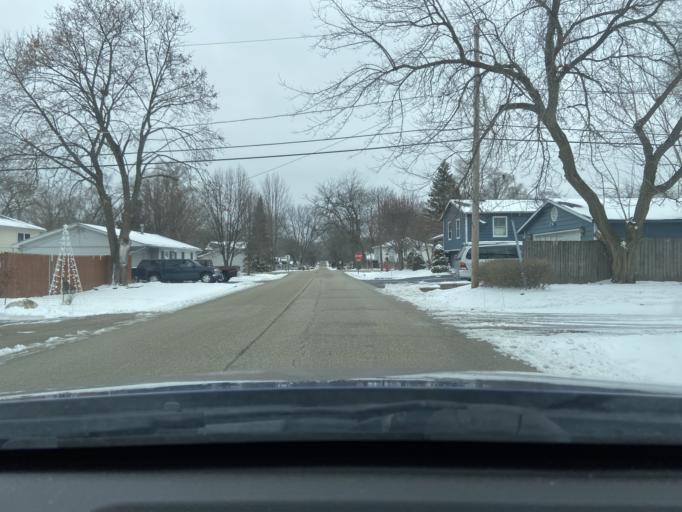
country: US
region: Illinois
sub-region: Lake County
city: Round Lake Park
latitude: 42.3509
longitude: -88.0797
